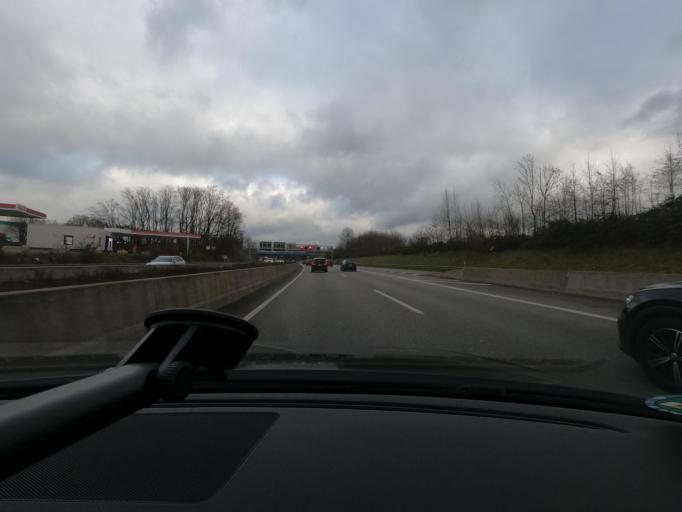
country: DE
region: North Rhine-Westphalia
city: Bochum-Hordel
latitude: 51.4852
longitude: 7.1831
